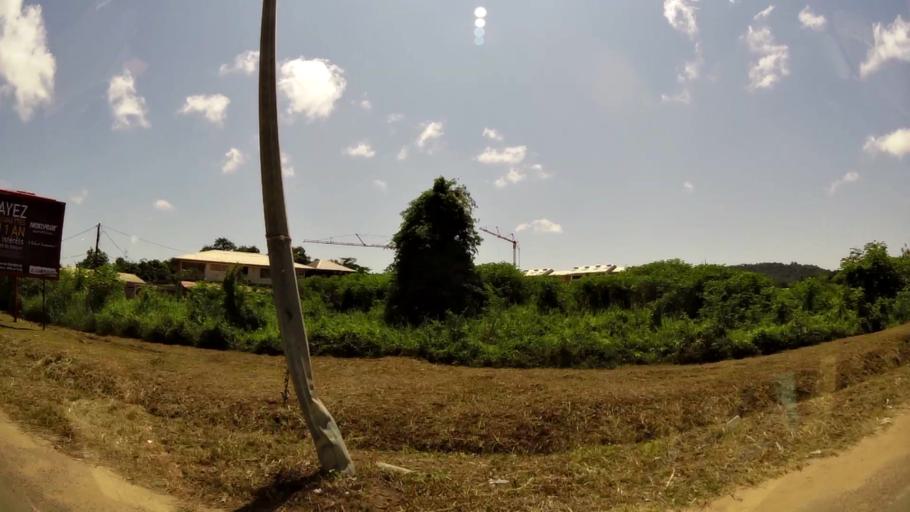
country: GF
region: Guyane
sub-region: Guyane
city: Cayenne
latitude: 4.9162
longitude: -52.3211
